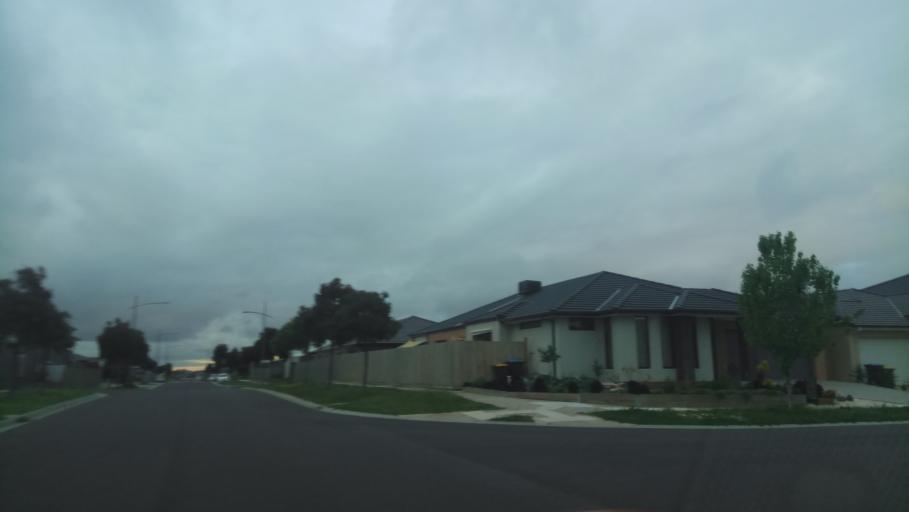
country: AU
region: Victoria
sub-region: Wyndham
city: Point Cook
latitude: -37.9074
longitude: 144.7589
